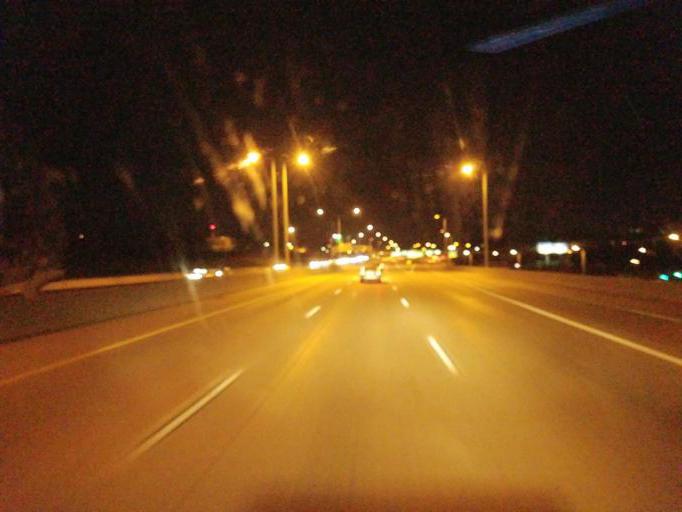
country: US
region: Iowa
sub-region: Polk County
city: Des Moines
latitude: 41.5959
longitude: -93.6365
